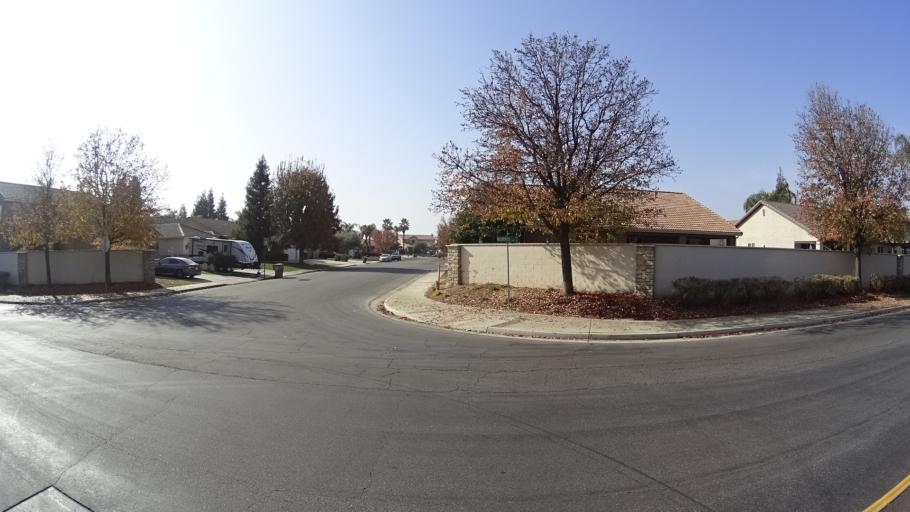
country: US
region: California
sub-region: Kern County
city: Greenacres
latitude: 35.4253
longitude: -119.1185
